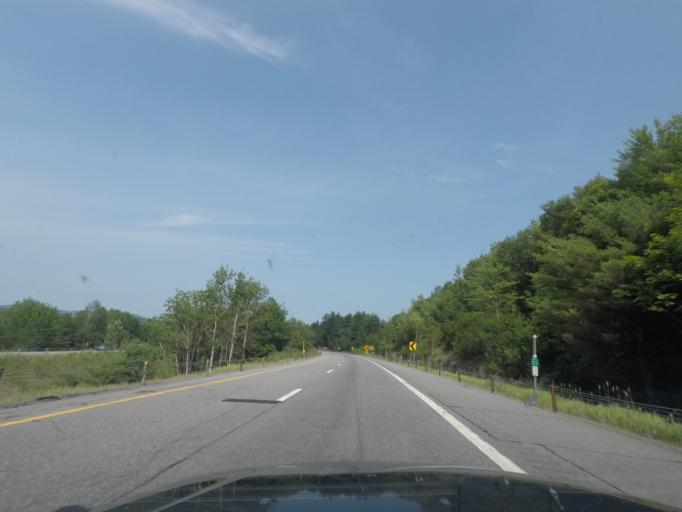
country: US
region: New York
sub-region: Essex County
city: Elizabethtown
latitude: 44.1915
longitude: -73.5448
